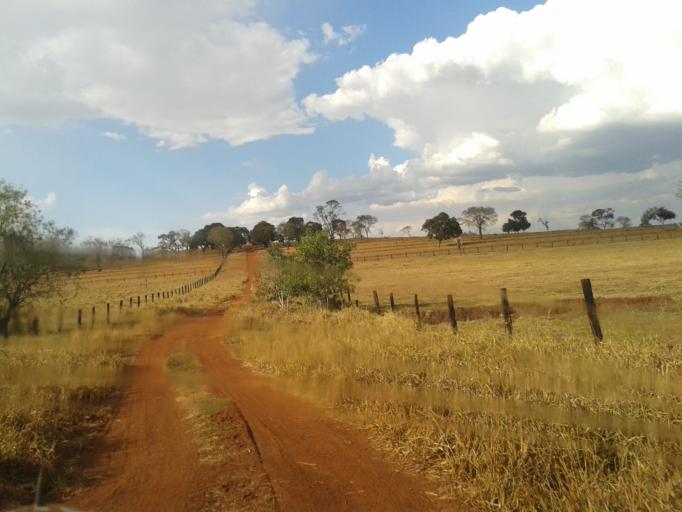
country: BR
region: Minas Gerais
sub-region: Santa Vitoria
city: Santa Vitoria
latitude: -19.1772
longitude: -49.9796
